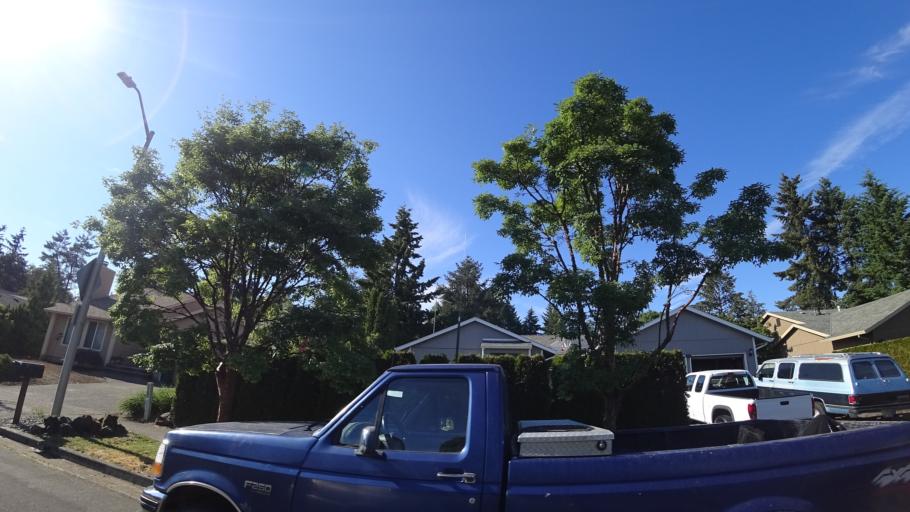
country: US
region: Oregon
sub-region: Washington County
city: Beaverton
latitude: 45.4577
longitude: -122.8129
